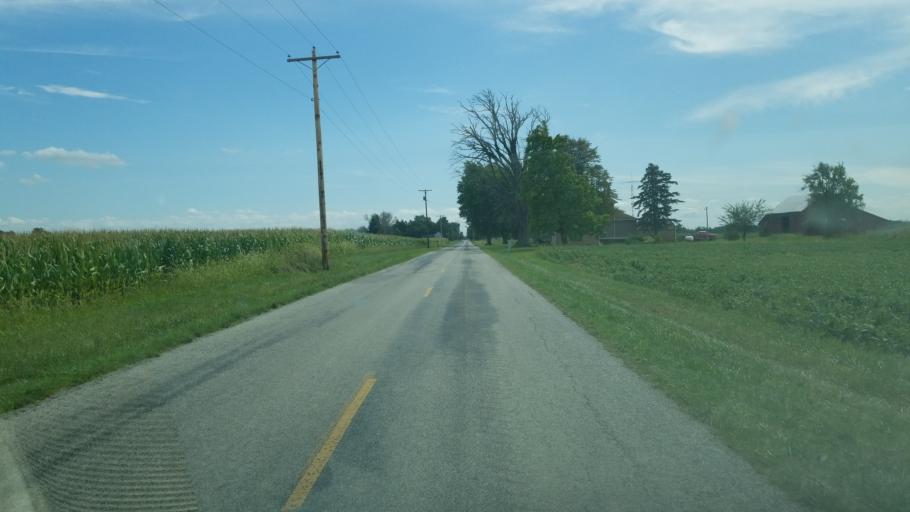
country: US
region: Ohio
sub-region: Union County
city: Richwood
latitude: 40.5971
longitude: -83.3147
